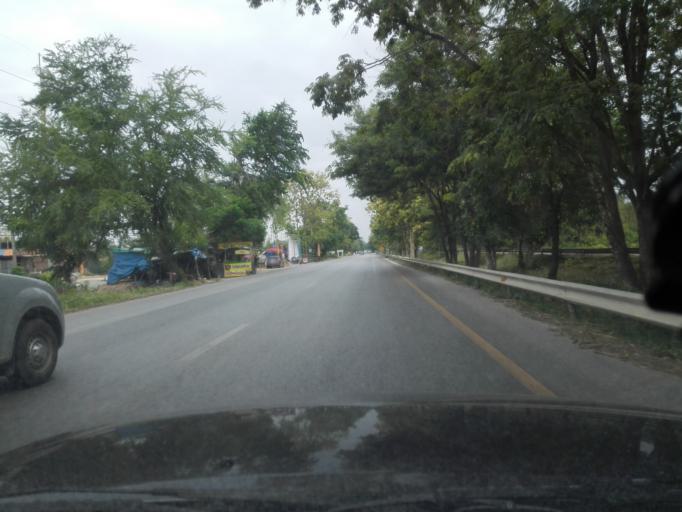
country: TH
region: Nakhon Sawan
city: Nakhon Sawan
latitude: 15.7293
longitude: 100.0365
